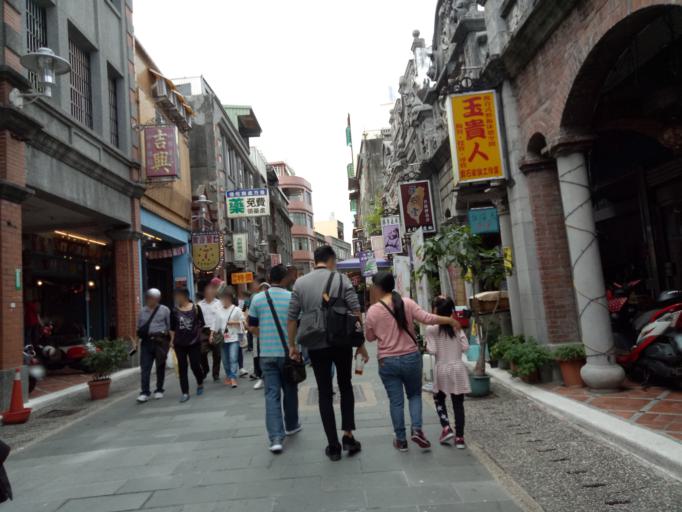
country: TW
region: Taiwan
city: Daxi
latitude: 24.8847
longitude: 121.2887
